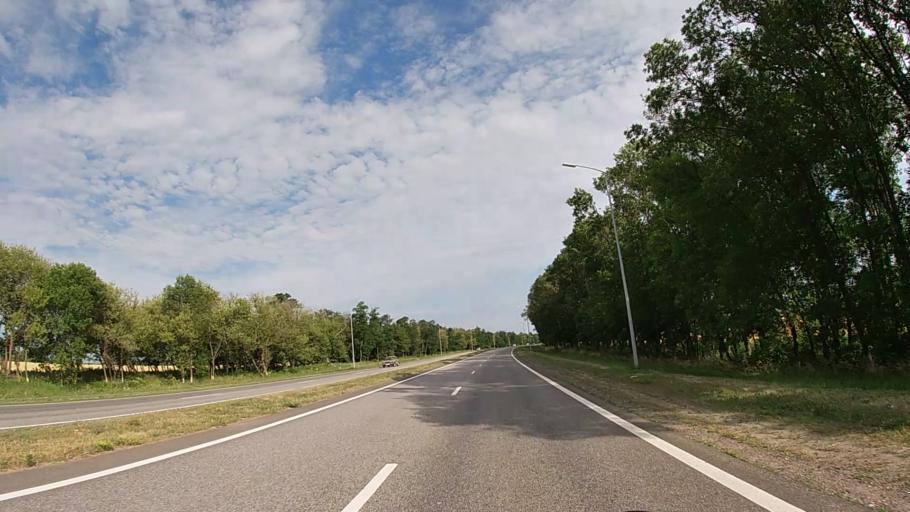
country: RU
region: Belgorod
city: Tomarovka
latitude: 50.6726
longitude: 36.2986
